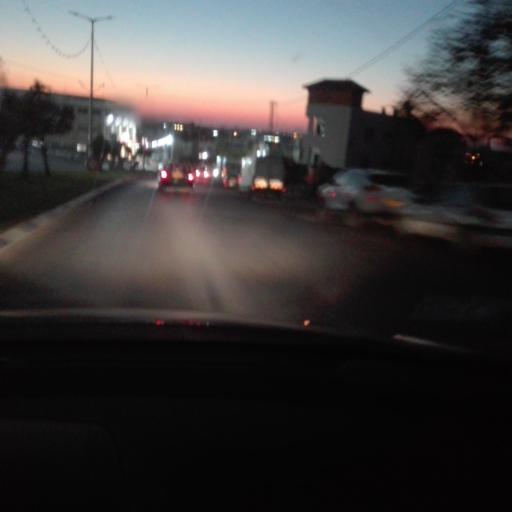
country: PS
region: West Bank
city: Nazlat `Isa
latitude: 32.4254
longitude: 35.0347
